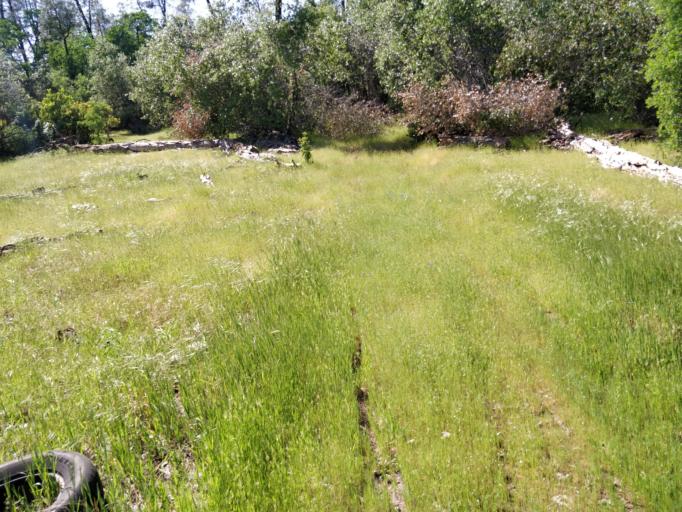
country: US
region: California
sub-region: Shasta County
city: Shasta Lake
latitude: 40.6673
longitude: -122.3677
